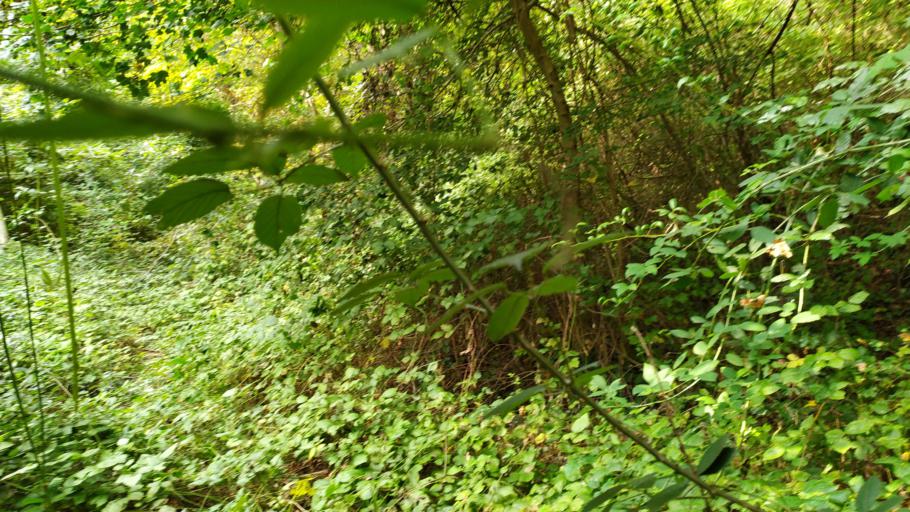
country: IT
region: Friuli Venezia Giulia
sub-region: Provincia di Pordenone
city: Aviano-Castello
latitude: 46.0744
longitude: 12.5740
